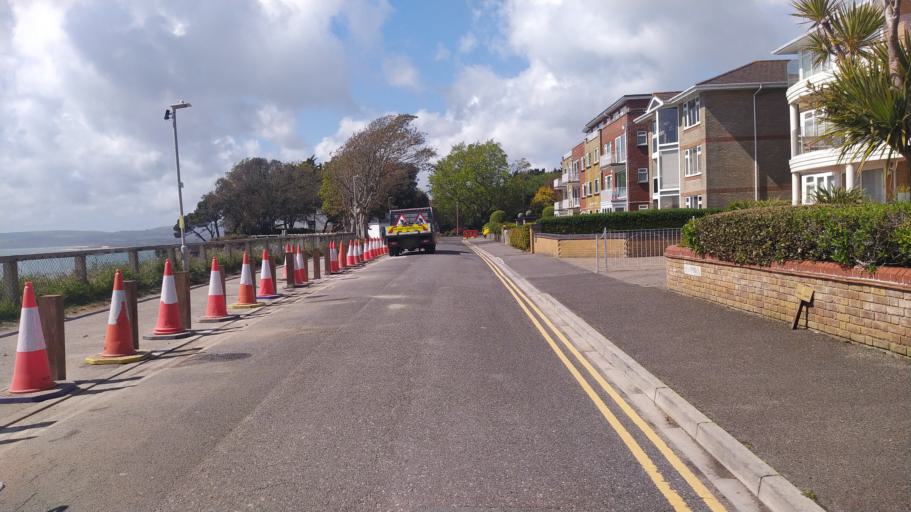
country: GB
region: England
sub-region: Dorset
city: Parkstone
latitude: 50.6997
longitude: -1.9236
